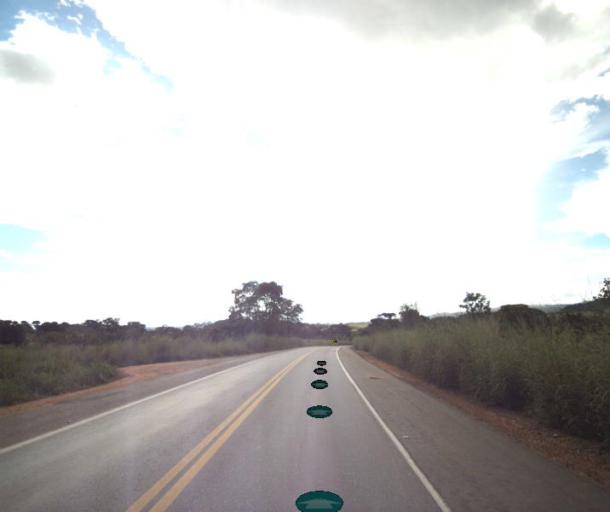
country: BR
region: Goias
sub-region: Jaragua
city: Jaragua
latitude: -15.6575
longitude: -49.3600
